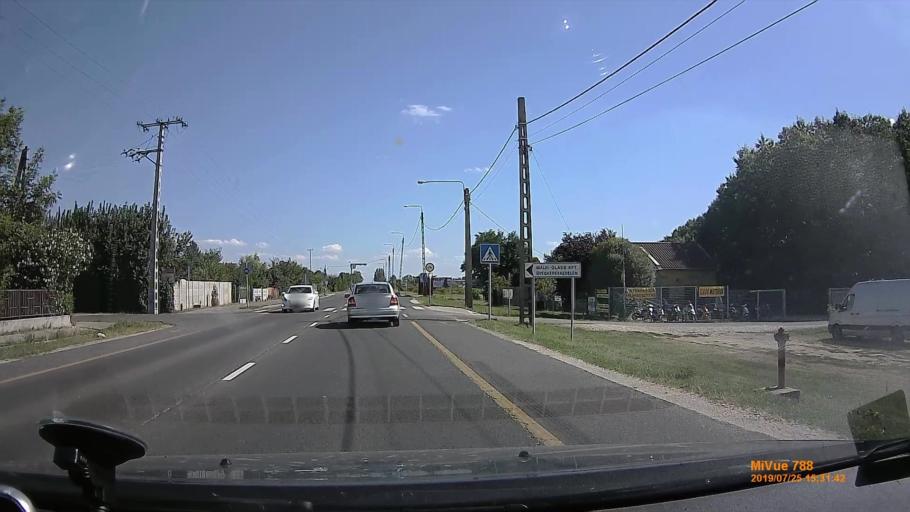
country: HU
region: Borsod-Abauj-Zemplen
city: Malyi
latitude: 48.0117
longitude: 20.8252
